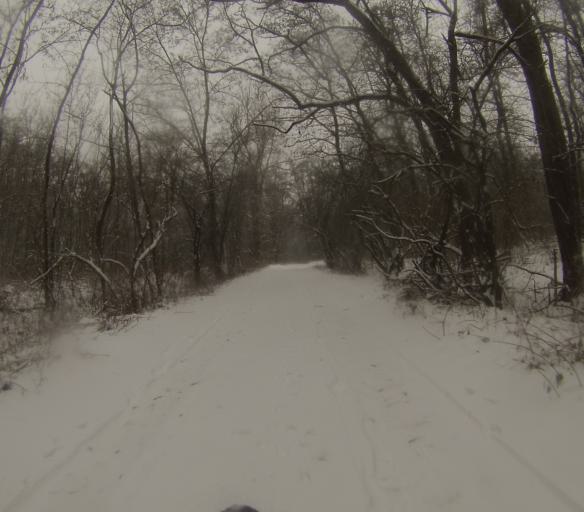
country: CZ
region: South Moravian
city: Orechov
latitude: 49.1319
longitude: 16.5366
